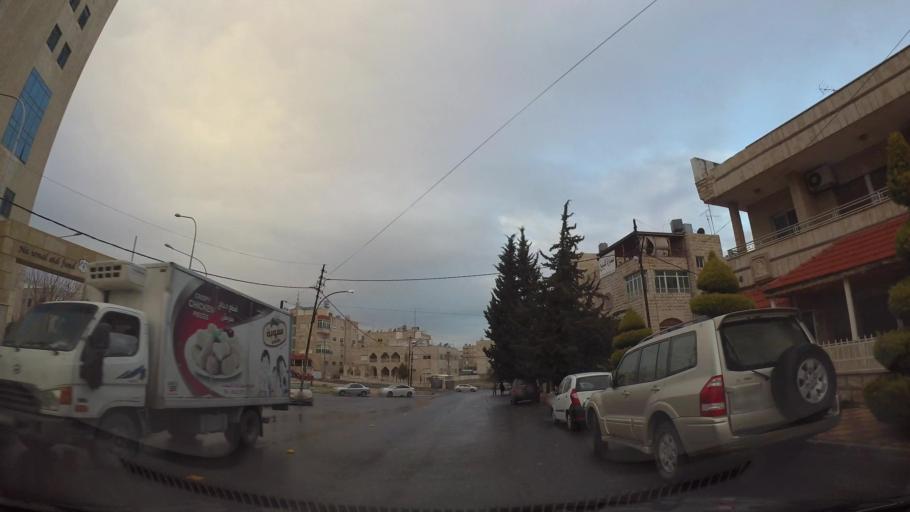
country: JO
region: Amman
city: Amman
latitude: 31.9768
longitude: 35.9118
